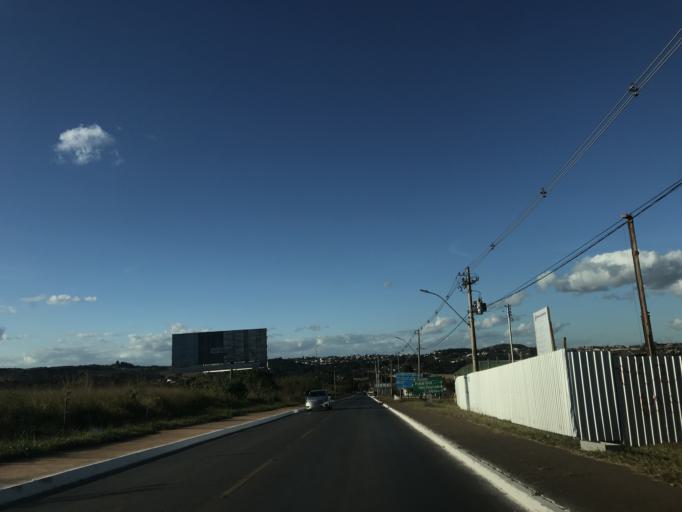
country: BR
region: Federal District
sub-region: Brasilia
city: Brasilia
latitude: -15.8929
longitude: -47.7836
